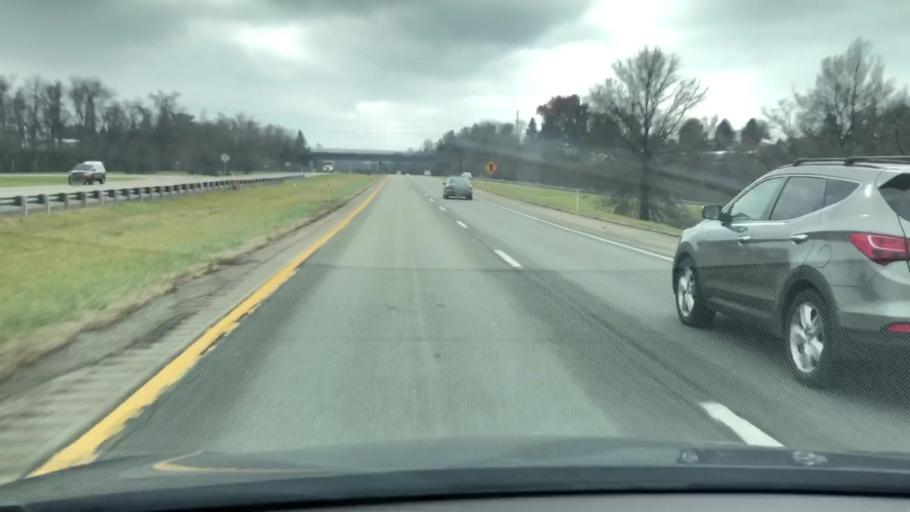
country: US
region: Pennsylvania
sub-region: Fayette County
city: South Uniontown
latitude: 39.8988
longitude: -79.7502
